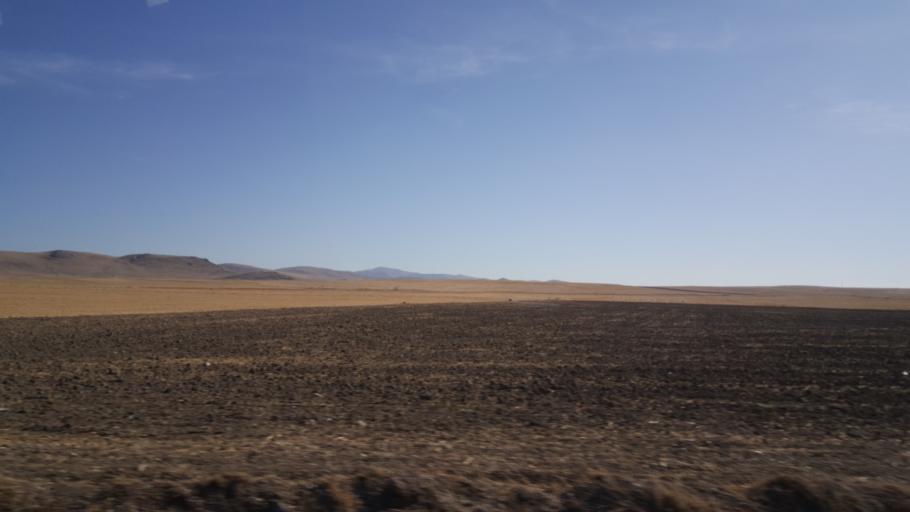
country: TR
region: Ankara
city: Yenice
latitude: 39.3473
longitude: 32.7639
